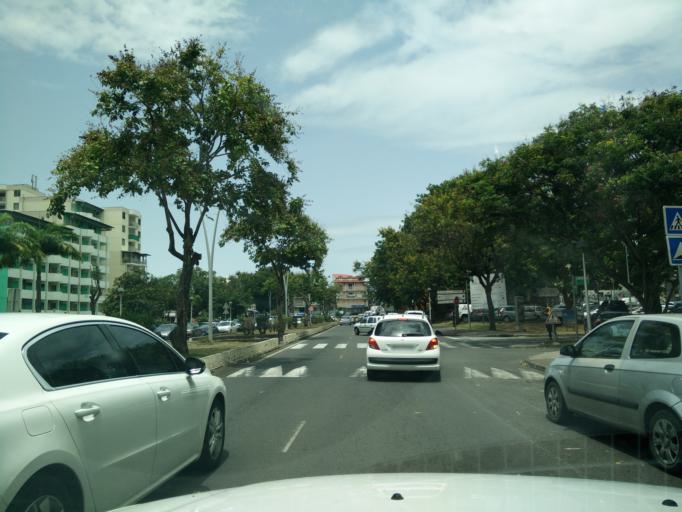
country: GP
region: Guadeloupe
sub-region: Guadeloupe
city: Pointe-a-Pitre
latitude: 16.2412
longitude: -61.5317
